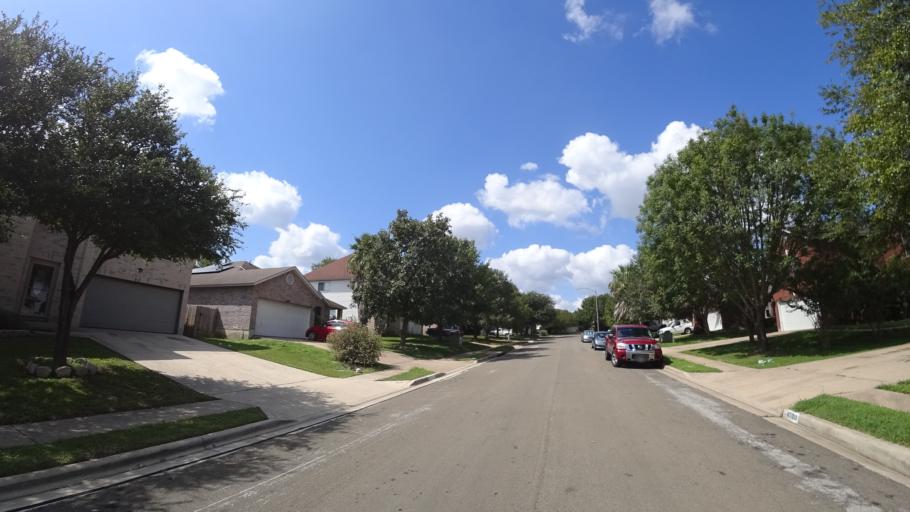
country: US
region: Texas
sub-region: Travis County
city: Manchaca
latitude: 30.1863
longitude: -97.8142
